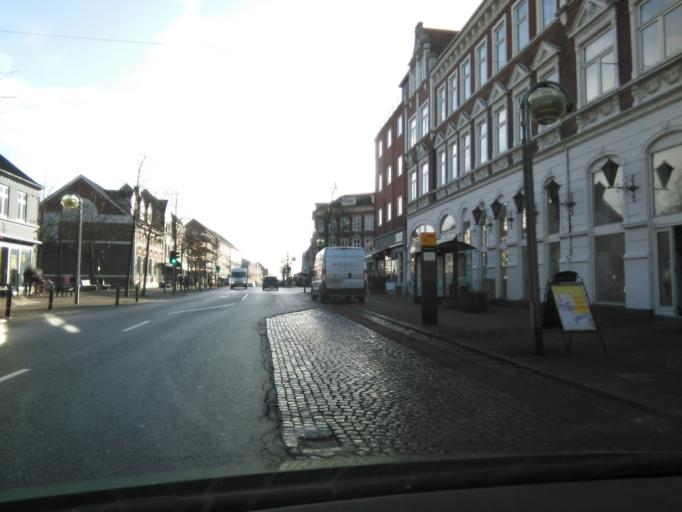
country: DK
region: Central Jutland
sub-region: Skanderborg Kommune
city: Skanderborg
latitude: 56.0354
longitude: 9.9311
